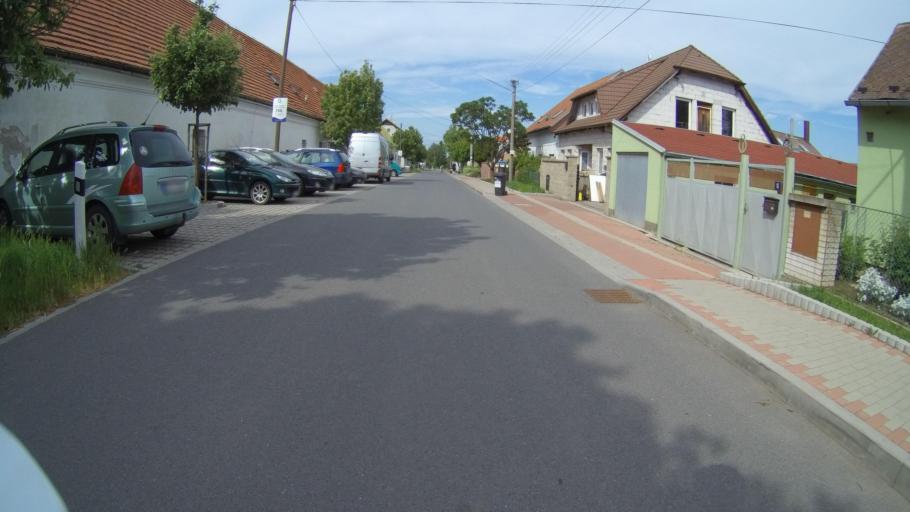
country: CZ
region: Central Bohemia
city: Libeznice
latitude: 50.1805
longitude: 14.4799
